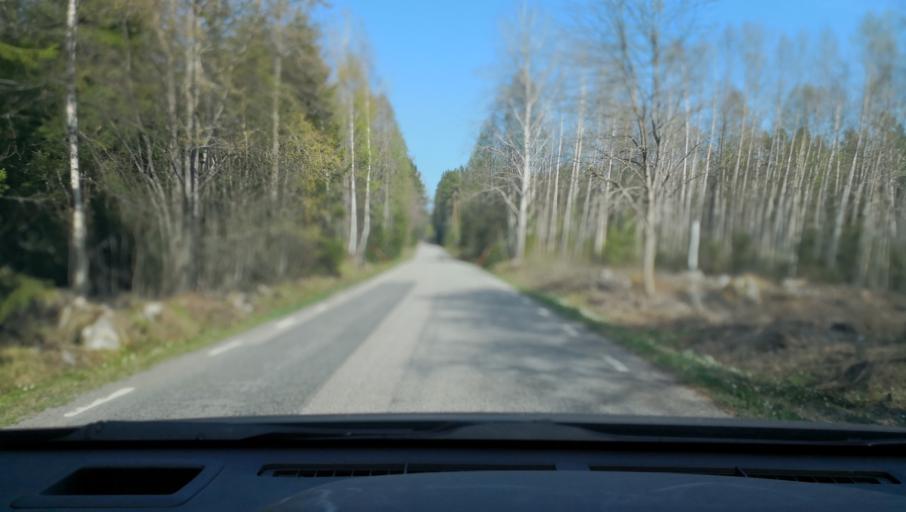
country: SE
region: Uppsala
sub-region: Heby Kommun
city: Heby
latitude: 60.0445
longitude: 16.8458
